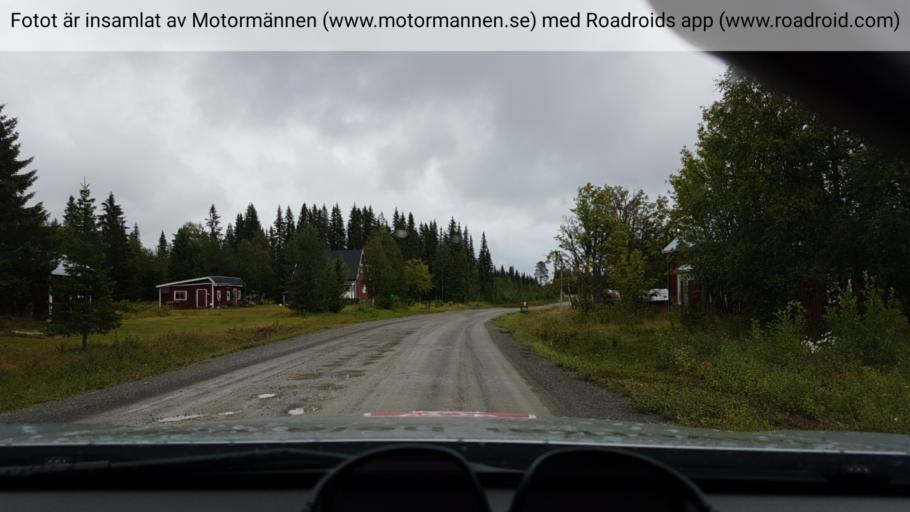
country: SE
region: Vaesterbotten
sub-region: Storumans Kommun
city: Storuman
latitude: 64.8549
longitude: 17.3967
